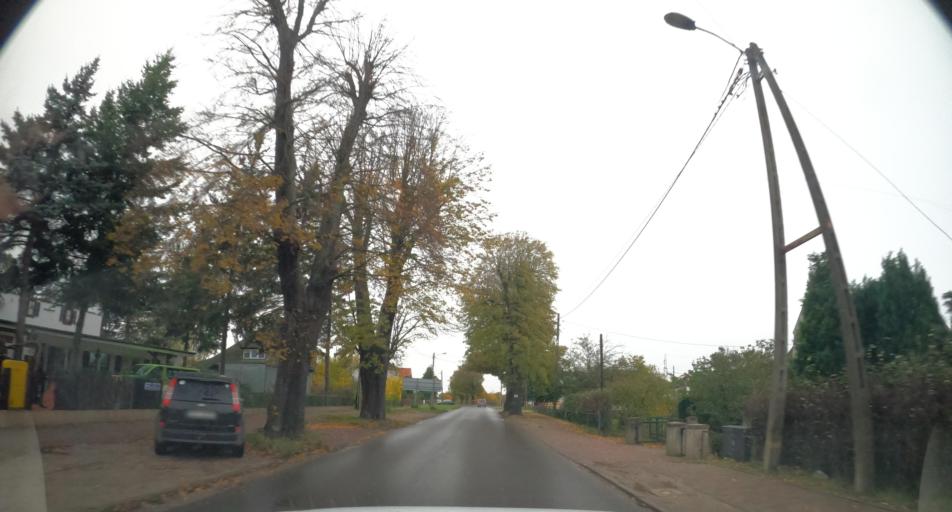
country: PL
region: West Pomeranian Voivodeship
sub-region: Powiat kamienski
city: Wolin
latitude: 53.8488
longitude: 14.6118
